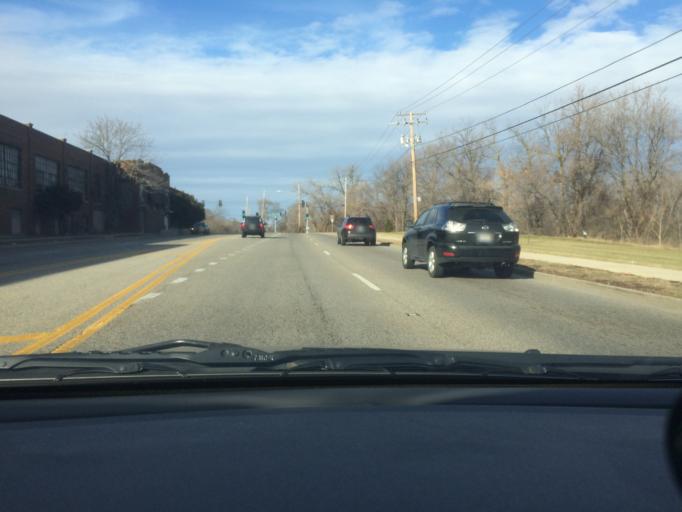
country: US
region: Illinois
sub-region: Kane County
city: Elgin
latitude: 42.0437
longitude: -88.2927
